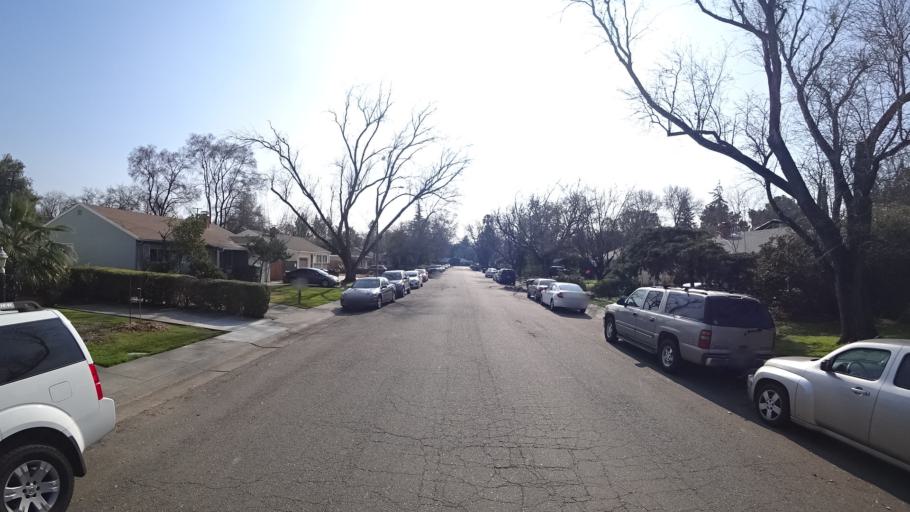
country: US
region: California
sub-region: Yolo County
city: Davis
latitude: 38.5523
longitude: -121.7514
